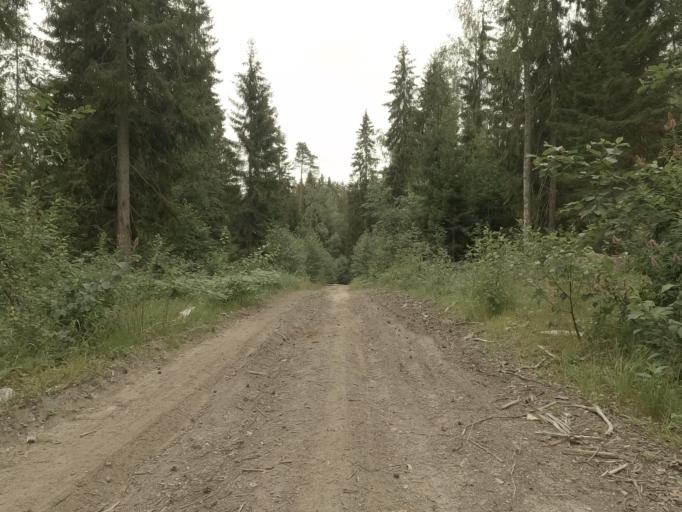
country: RU
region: Leningrad
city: Kamennogorsk
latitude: 61.0715
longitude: 29.1664
